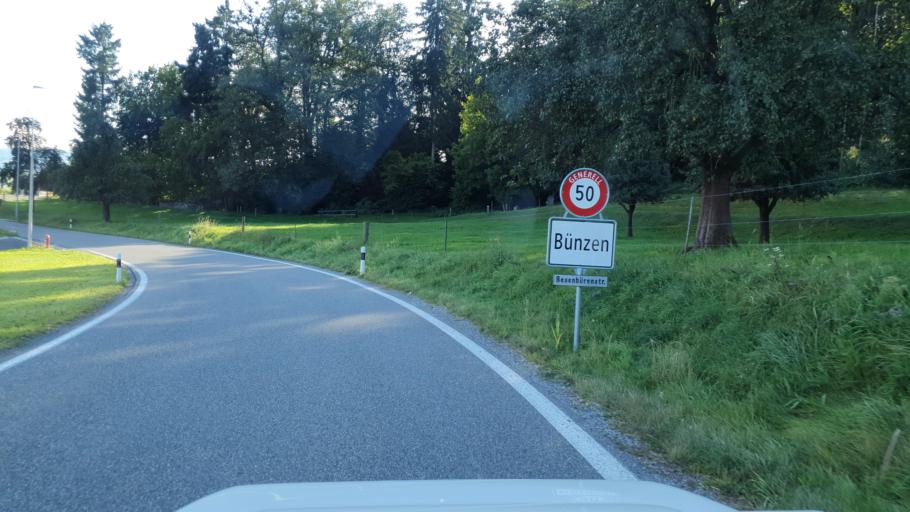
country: CH
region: Aargau
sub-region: Bezirk Muri
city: Waltenschwil
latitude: 47.3126
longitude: 8.3318
